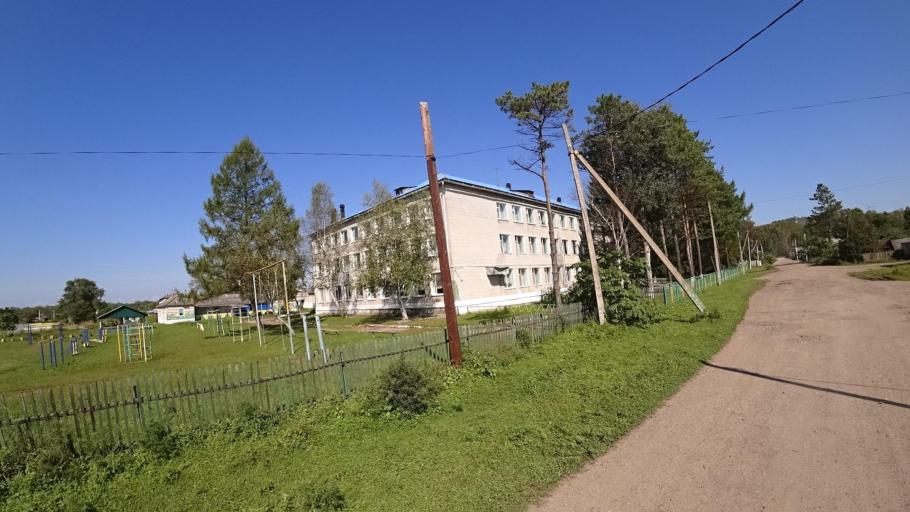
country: RU
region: Jewish Autonomous Oblast
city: Bira
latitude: 48.9969
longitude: 132.4549
